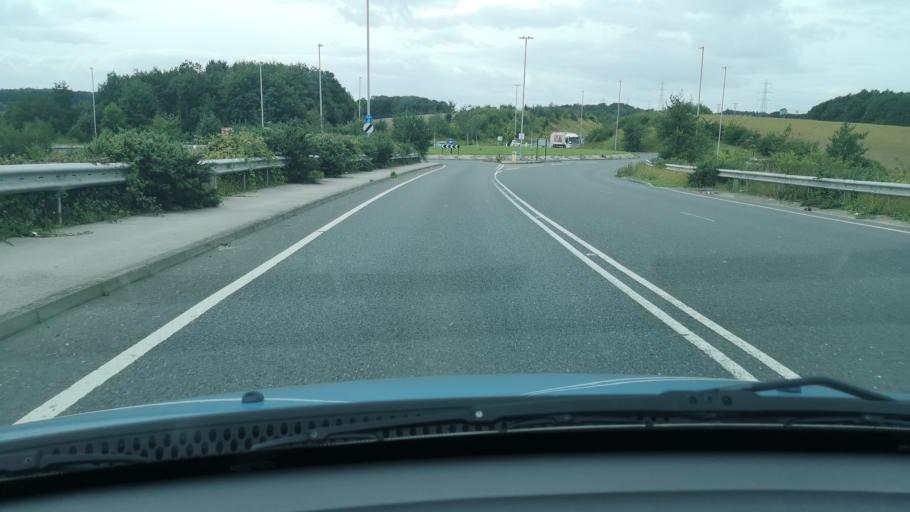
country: GB
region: England
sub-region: City and Borough of Wakefield
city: Hemsworth
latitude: 53.6055
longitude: -1.3290
